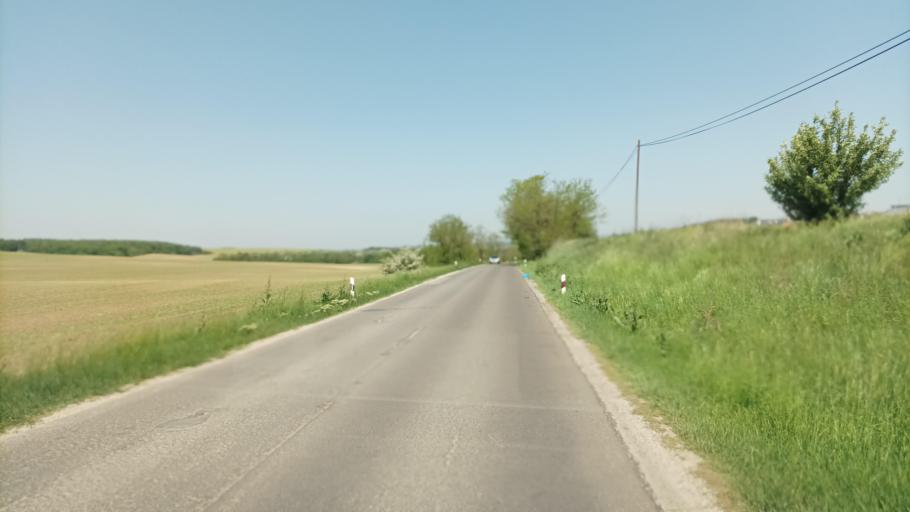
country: HU
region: Pest
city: Pecel
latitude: 47.4645
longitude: 19.3455
